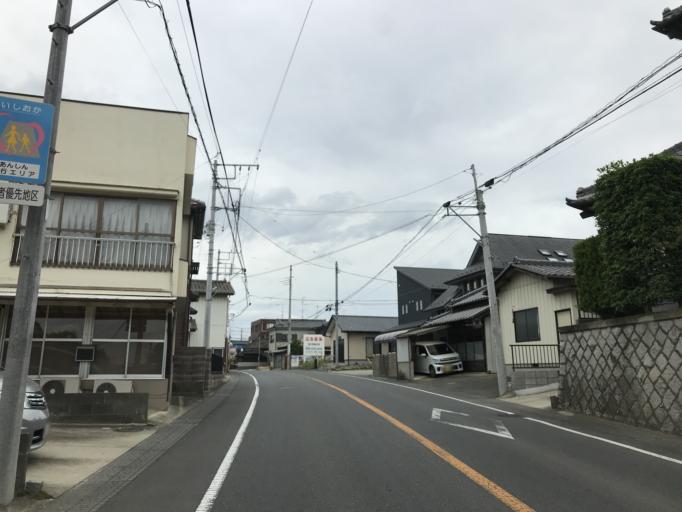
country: JP
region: Ibaraki
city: Ishioka
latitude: 36.1843
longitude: 140.2734
